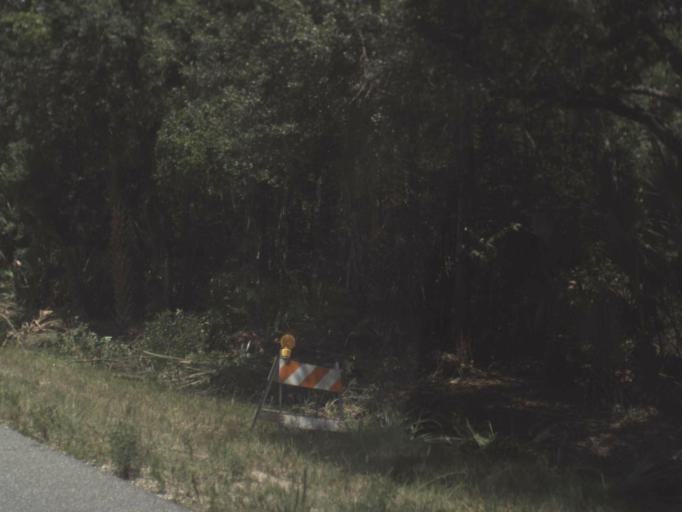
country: US
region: Florida
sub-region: Leon County
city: Woodville
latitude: 30.1438
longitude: -83.9418
